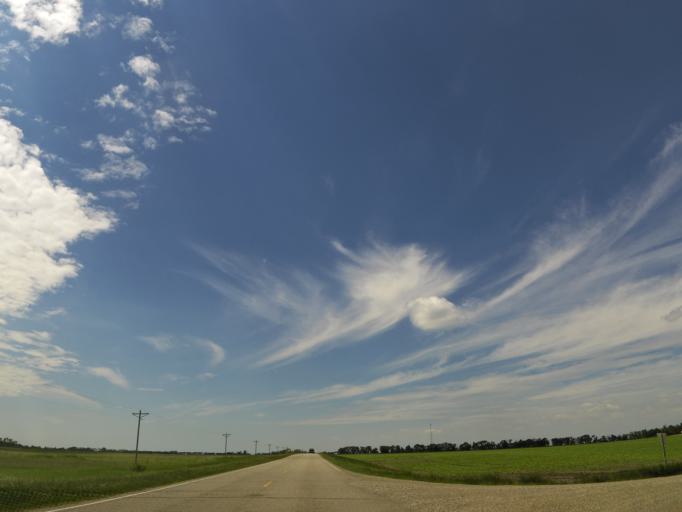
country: US
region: North Dakota
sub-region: Walsh County
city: Grafton
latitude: 48.2953
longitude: -97.2107
